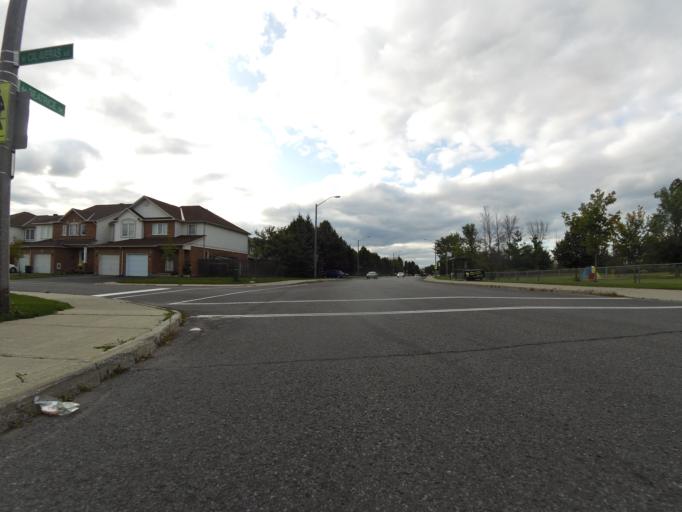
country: CA
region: Ontario
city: Bells Corners
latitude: 45.2813
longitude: -75.7298
